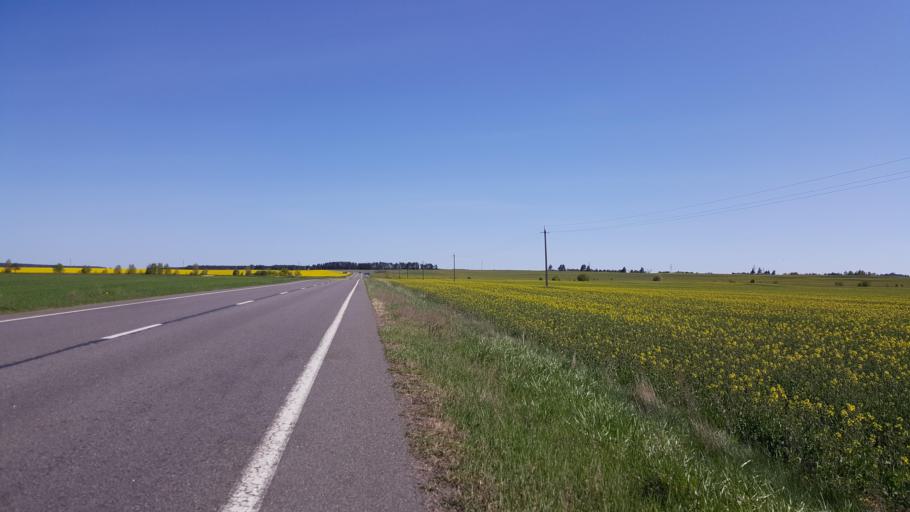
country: BY
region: Brest
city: Kamyanyets
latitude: 52.4144
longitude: 23.8499
